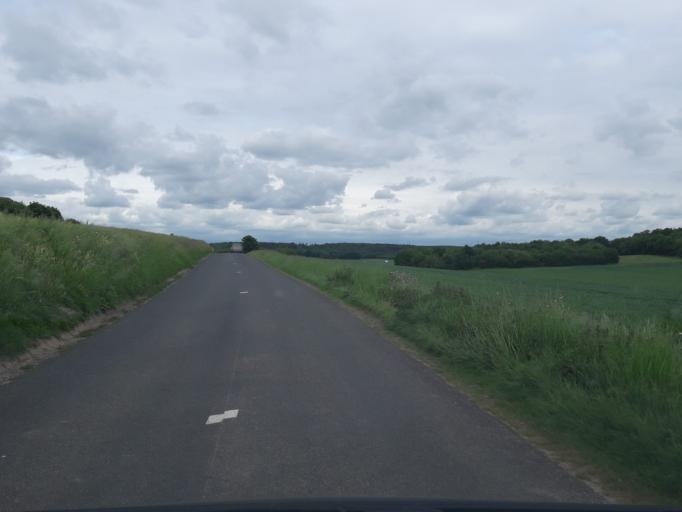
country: FR
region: Ile-de-France
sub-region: Departement de l'Essonne
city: Boissy-le-Cutte
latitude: 48.4109
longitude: 2.2733
